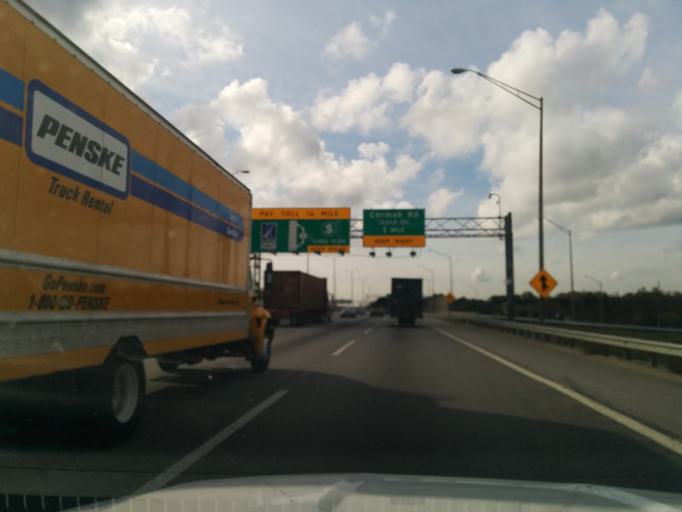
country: US
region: Illinois
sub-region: Cook County
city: Hillside
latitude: 41.8636
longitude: -87.9182
